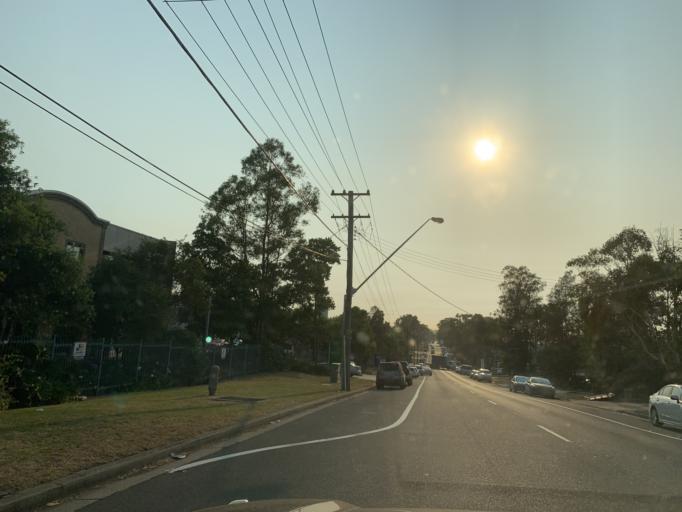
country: AU
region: New South Wales
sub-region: Fairfield
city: Horsley Park
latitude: -33.8375
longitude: 150.8817
